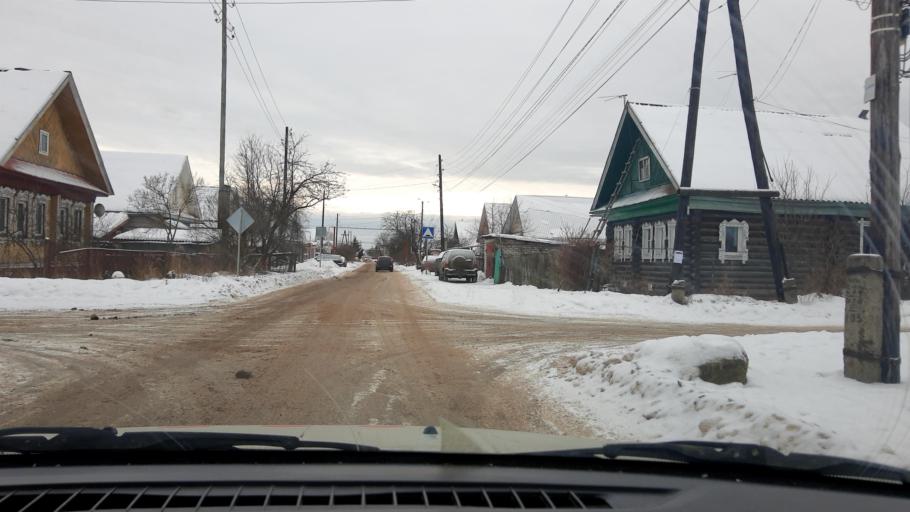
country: RU
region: Nizjnij Novgorod
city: Gorodets
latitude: 56.6661
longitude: 43.4779
